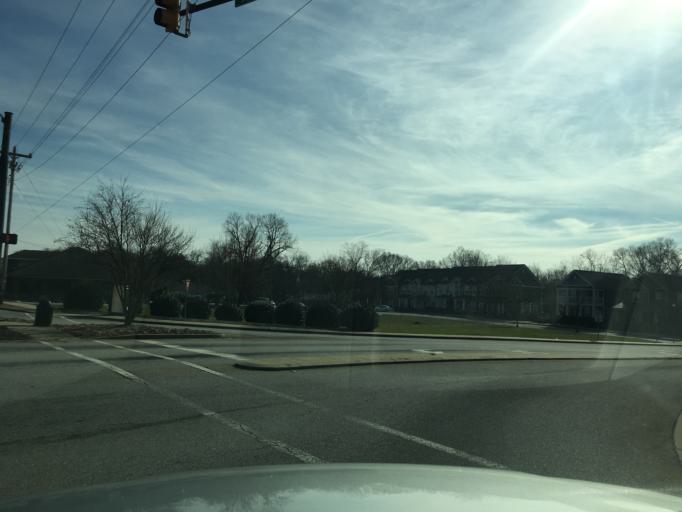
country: US
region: South Carolina
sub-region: Greenville County
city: Greenville
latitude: 34.8613
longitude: -82.4072
